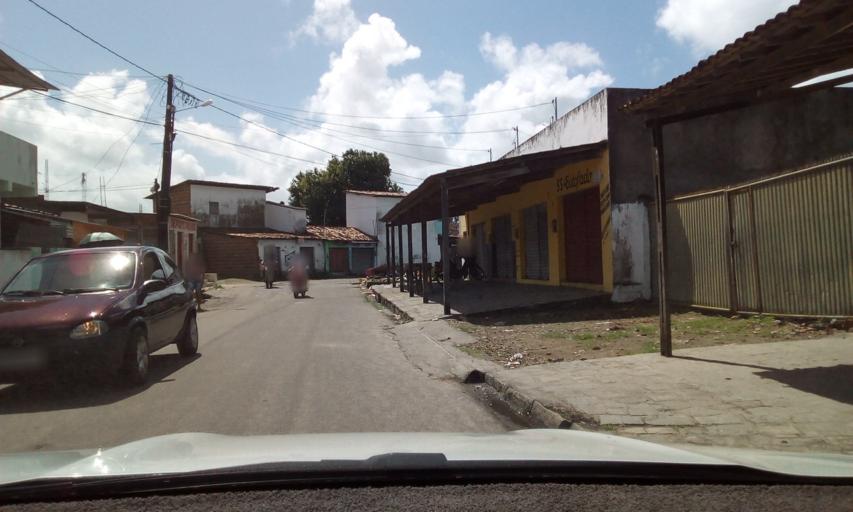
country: BR
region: Paraiba
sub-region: Bayeux
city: Bayeux
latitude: -7.1307
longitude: -34.9262
